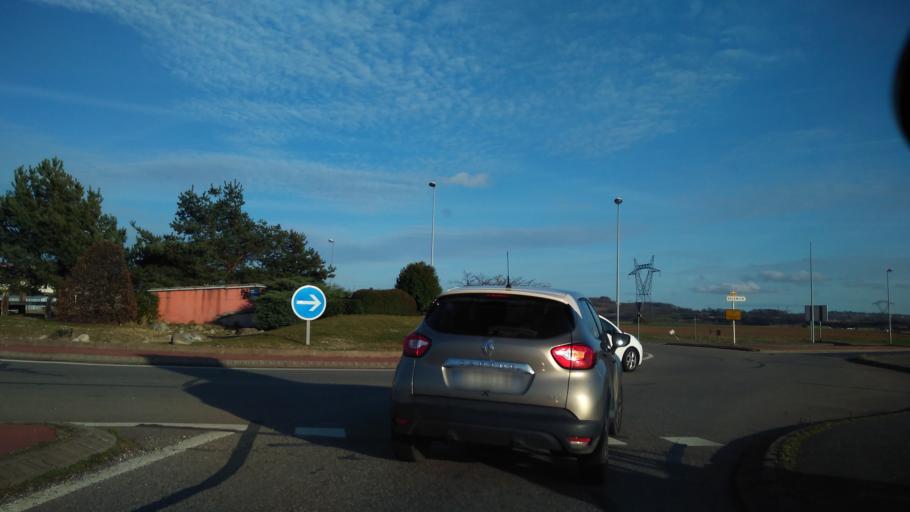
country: FR
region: Rhone-Alpes
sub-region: Departement du Rhone
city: Mions
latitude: 45.6519
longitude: 4.9535
